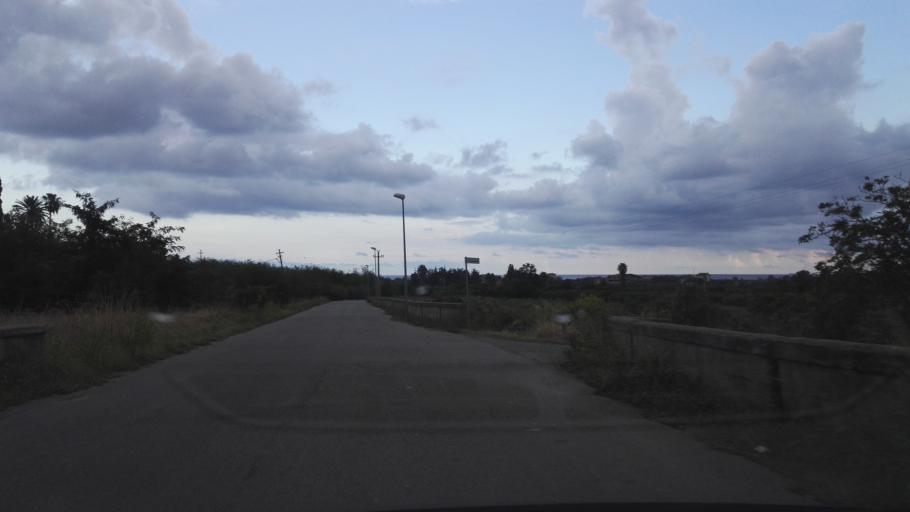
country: IT
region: Calabria
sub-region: Provincia di Reggio Calabria
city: Caulonia Marina
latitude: 38.3614
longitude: 16.4642
